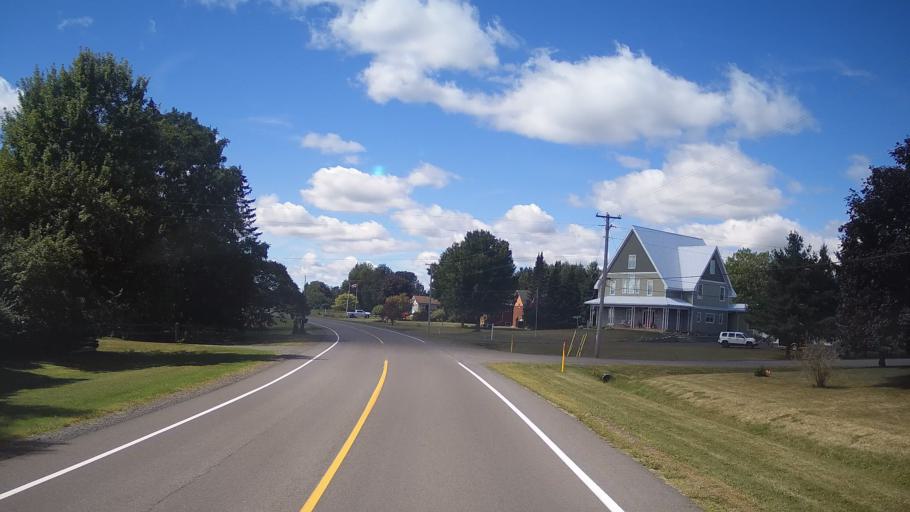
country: US
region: New York
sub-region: St. Lawrence County
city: Ogdensburg
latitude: 44.8611
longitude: -75.2637
